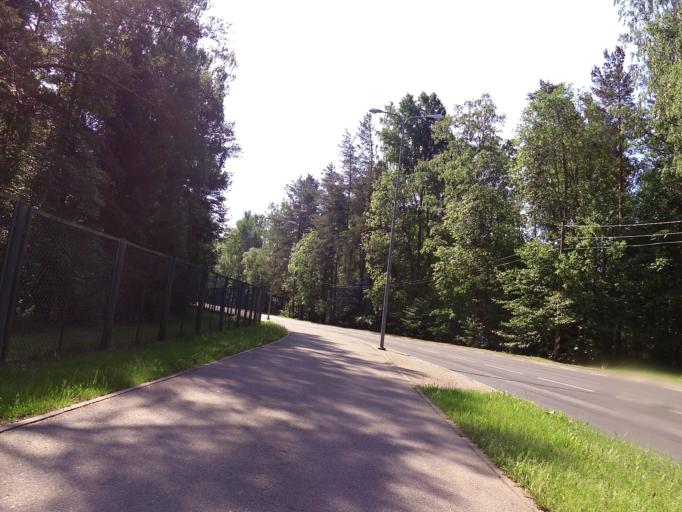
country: EE
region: Harju
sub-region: Saue vald
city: Laagri
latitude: 59.4342
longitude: 24.6296
